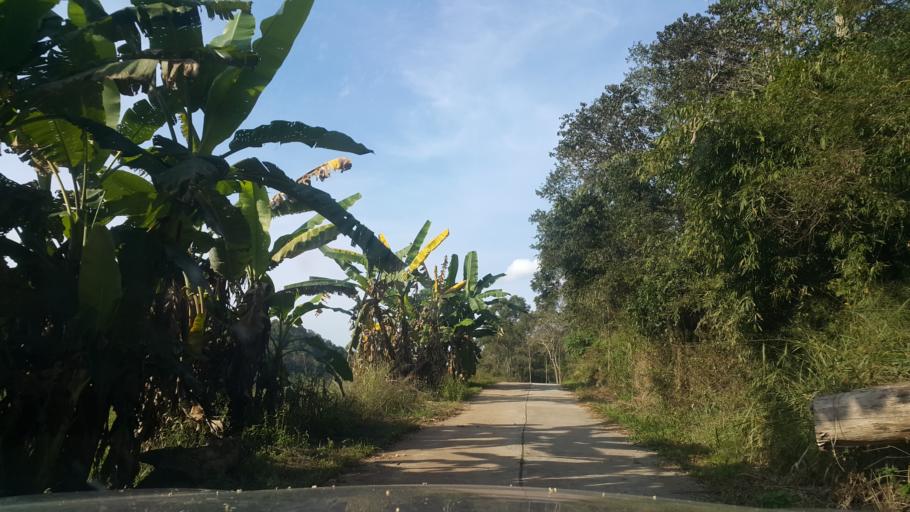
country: TH
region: Chiang Mai
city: Samoeng
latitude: 18.9877
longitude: 98.6849
